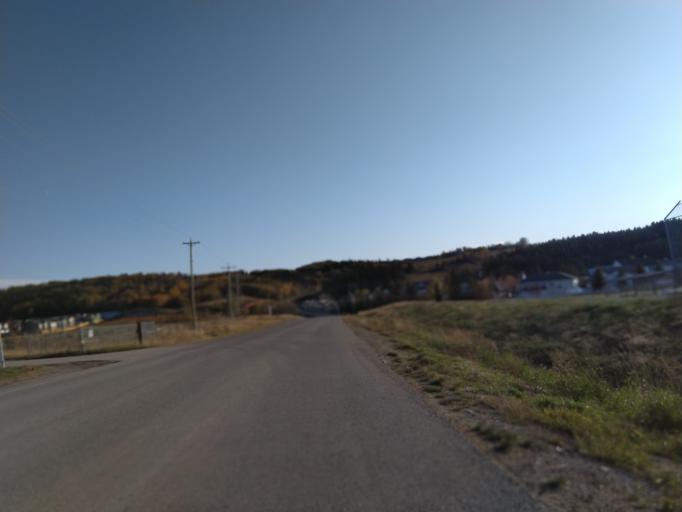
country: CA
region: Alberta
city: Cochrane
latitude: 51.1757
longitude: -114.4668
